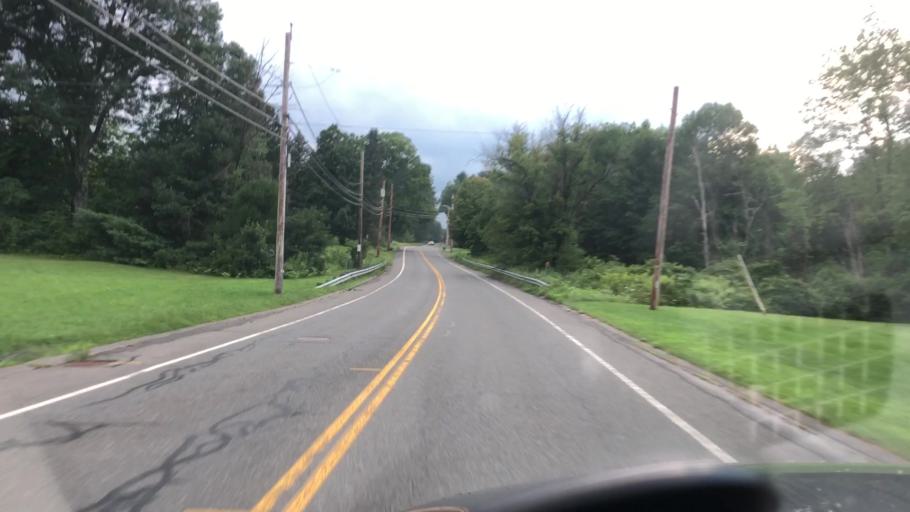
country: US
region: Massachusetts
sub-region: Hampshire County
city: Easthampton
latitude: 42.3020
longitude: -72.6948
